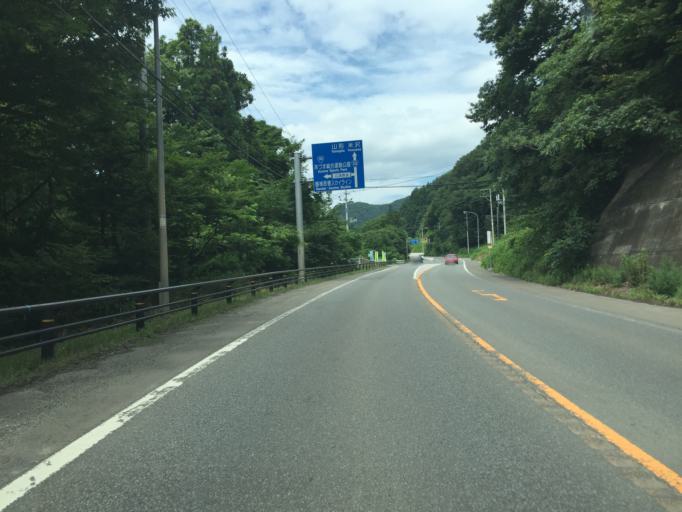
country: JP
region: Fukushima
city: Fukushima-shi
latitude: 37.8307
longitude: 140.3941
